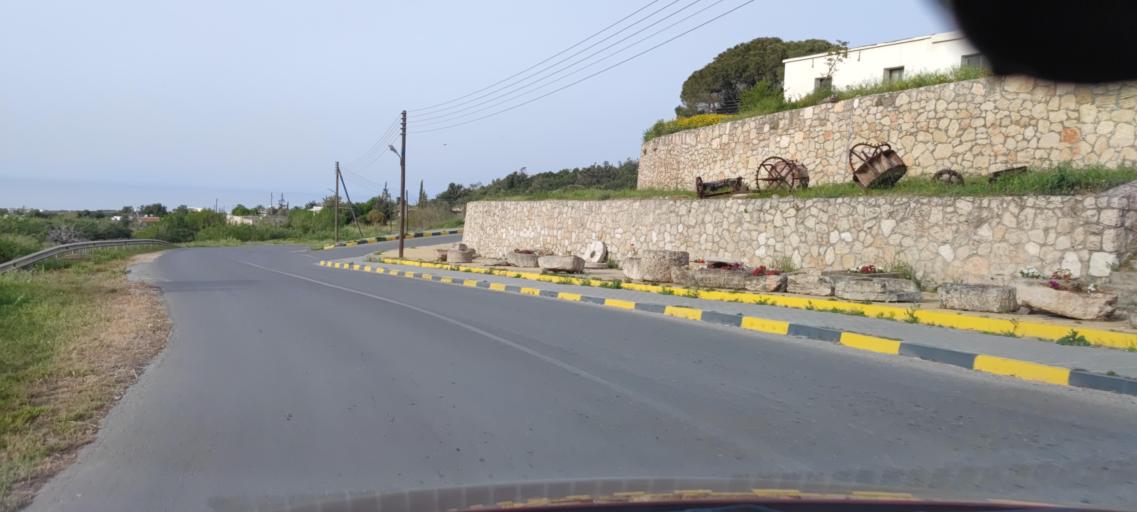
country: CY
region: Ammochostos
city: Leonarisso
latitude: 35.5358
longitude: 34.1924
